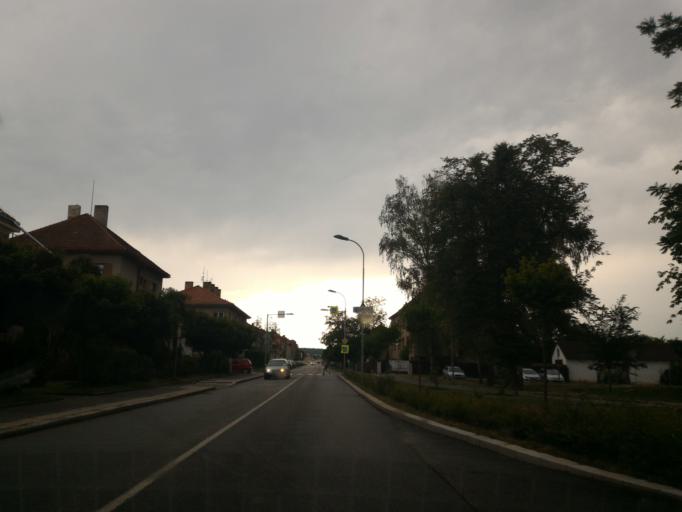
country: CZ
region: Vysocina
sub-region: Okres Jihlava
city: Telc
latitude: 49.1824
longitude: 15.4484
